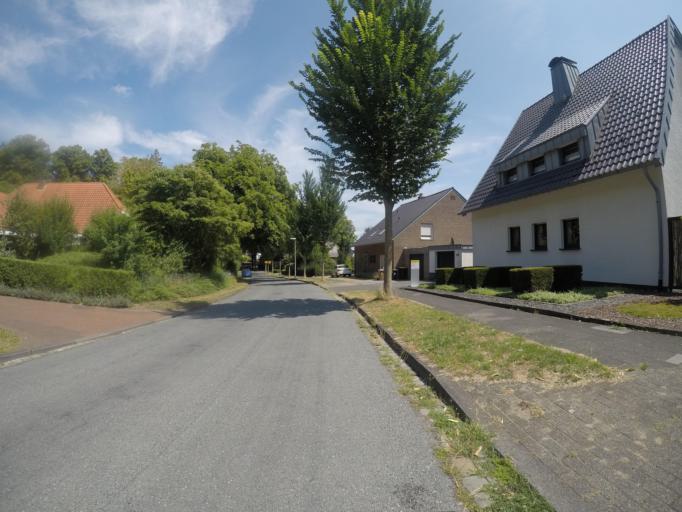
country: DE
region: North Rhine-Westphalia
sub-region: Regierungsbezirk Dusseldorf
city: Kleve
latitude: 51.7874
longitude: 6.1187
